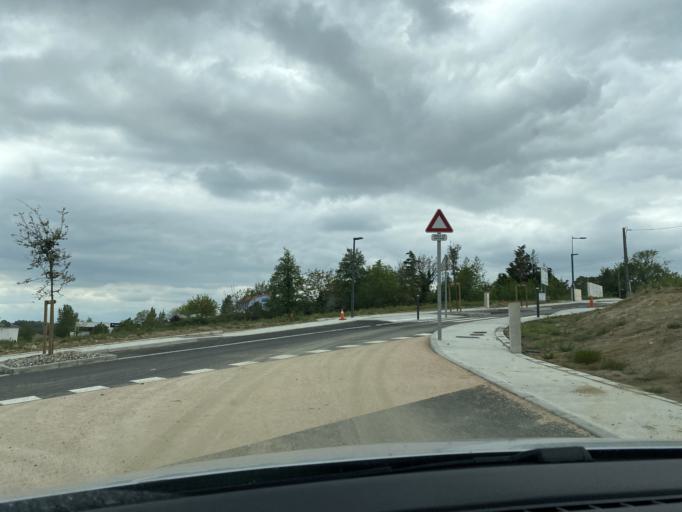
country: FR
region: Midi-Pyrenees
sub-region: Departement de la Haute-Garonne
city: Nailloux
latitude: 43.3656
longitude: 1.6244
